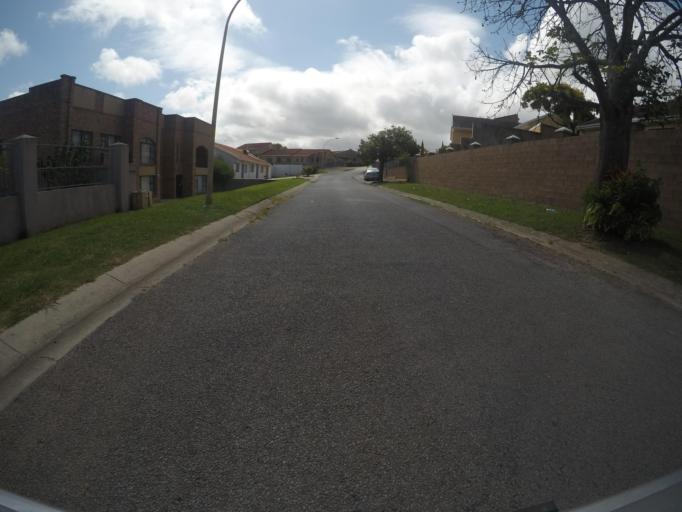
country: ZA
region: Eastern Cape
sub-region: Buffalo City Metropolitan Municipality
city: East London
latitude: -32.9987
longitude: 27.8870
